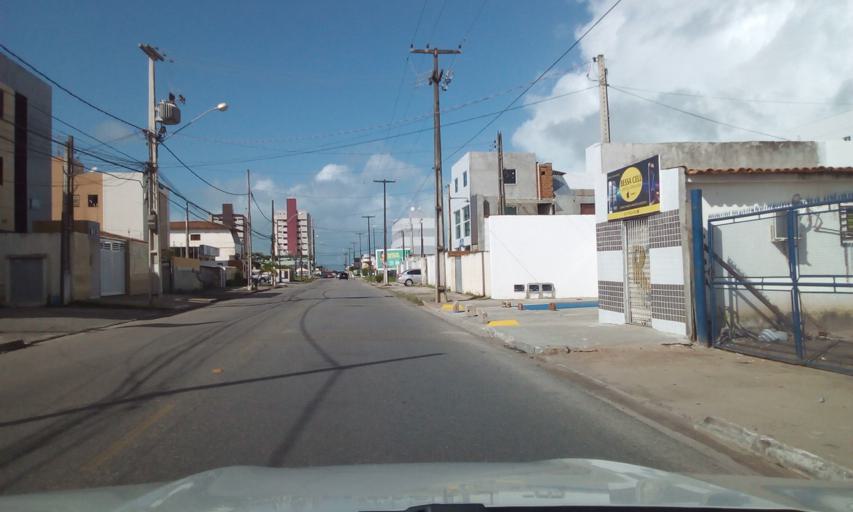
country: BR
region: Paraiba
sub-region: Joao Pessoa
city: Joao Pessoa
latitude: -7.0685
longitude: -34.8460
